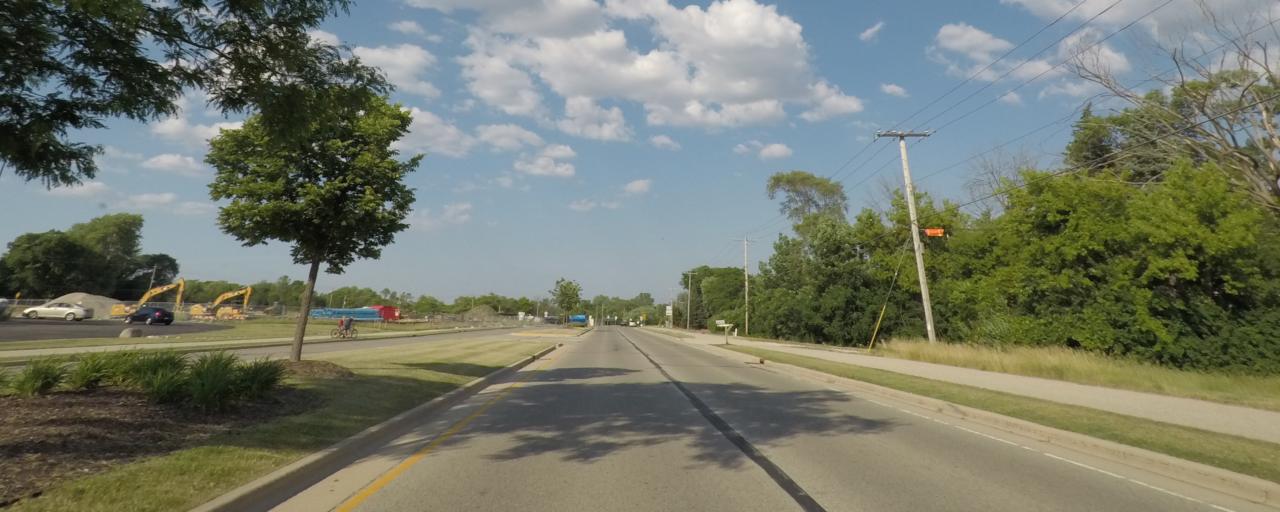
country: US
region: Wisconsin
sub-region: Milwaukee County
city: Hales Corners
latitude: 42.9284
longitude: -88.0846
